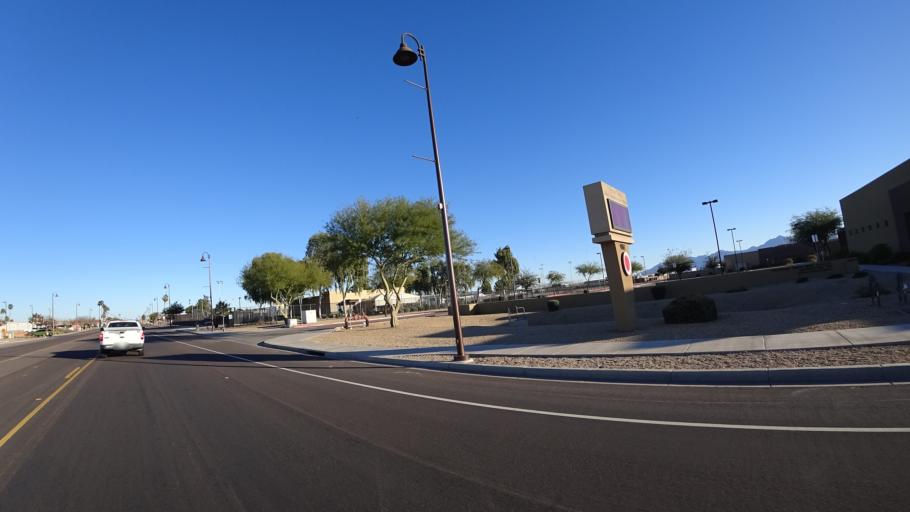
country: US
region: Arizona
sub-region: Maricopa County
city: Tolleson
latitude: 33.4502
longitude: -112.2692
